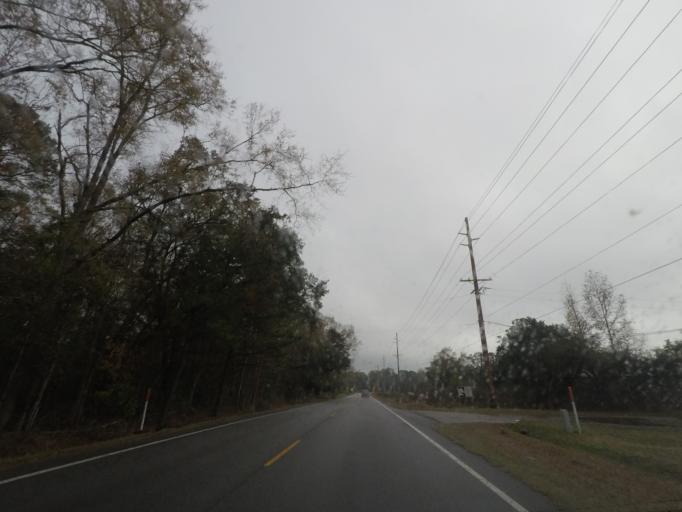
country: US
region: South Carolina
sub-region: Charleston County
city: Meggett
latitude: 32.6639
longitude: -80.3416
